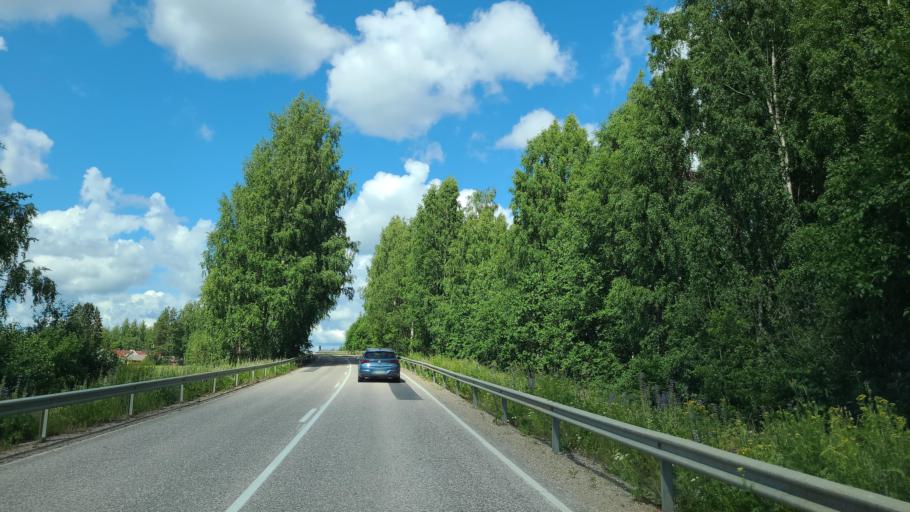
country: FI
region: Northern Savo
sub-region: Koillis-Savo
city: Kaavi
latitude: 62.9225
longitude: 28.6942
